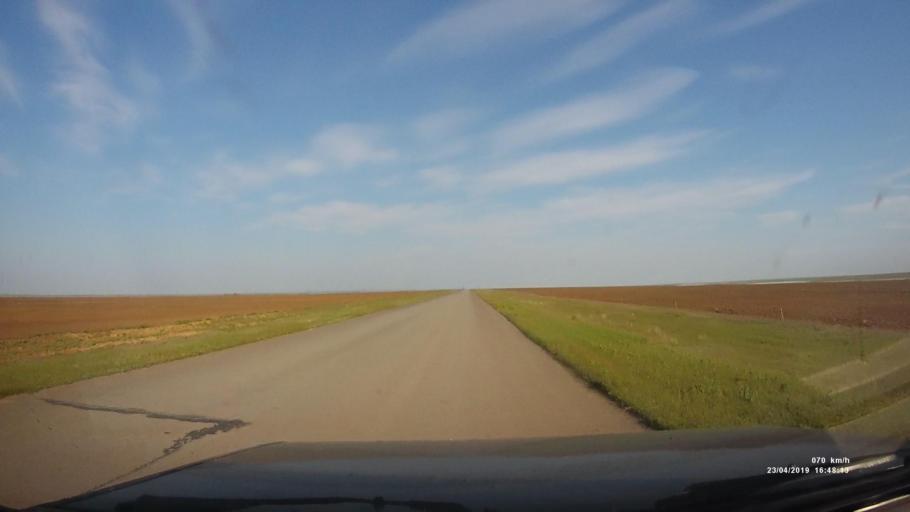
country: RU
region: Kalmykiya
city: Priyutnoye
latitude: 46.3359
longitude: 43.2586
